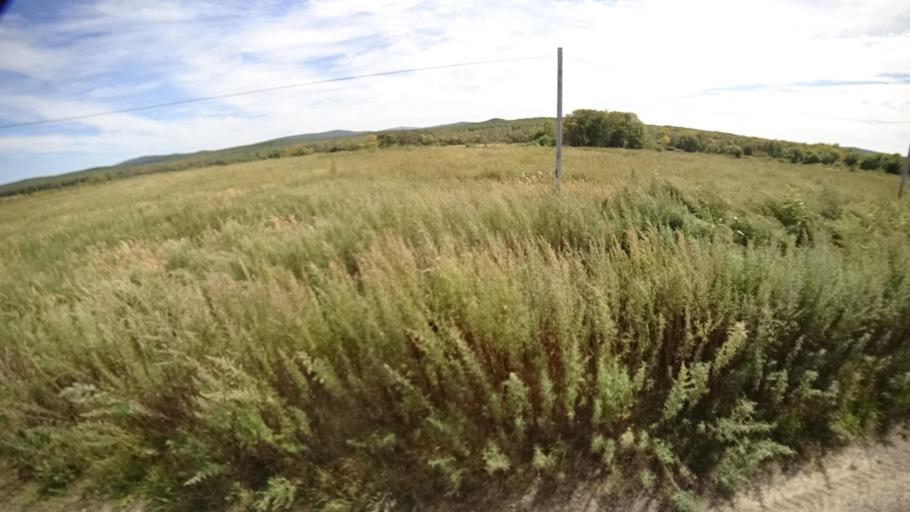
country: RU
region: Primorskiy
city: Yakovlevka
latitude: 44.6391
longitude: 133.5997
